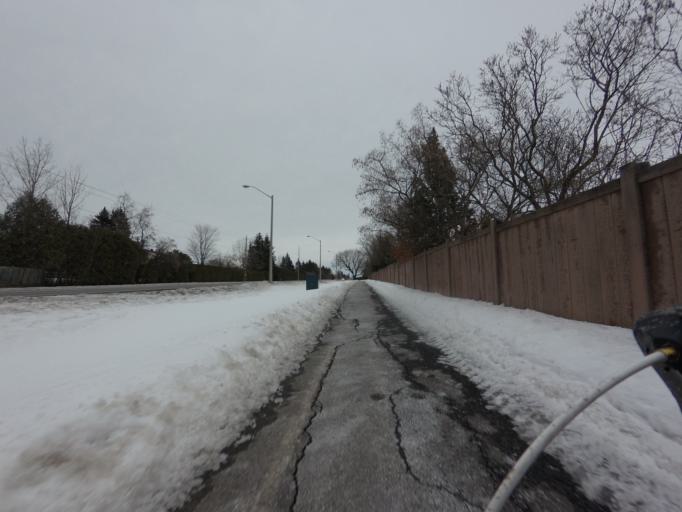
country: CA
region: Ontario
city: Bells Corners
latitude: 45.2753
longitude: -75.7693
